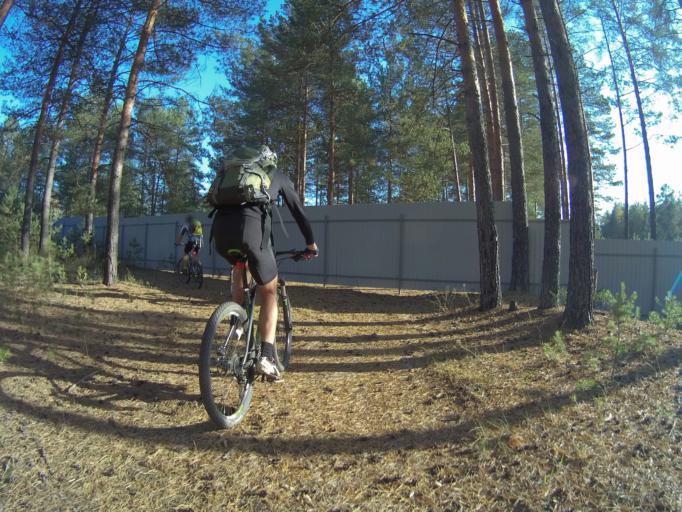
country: RU
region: Vladimir
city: Raduzhnyy
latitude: 56.0341
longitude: 40.3831
